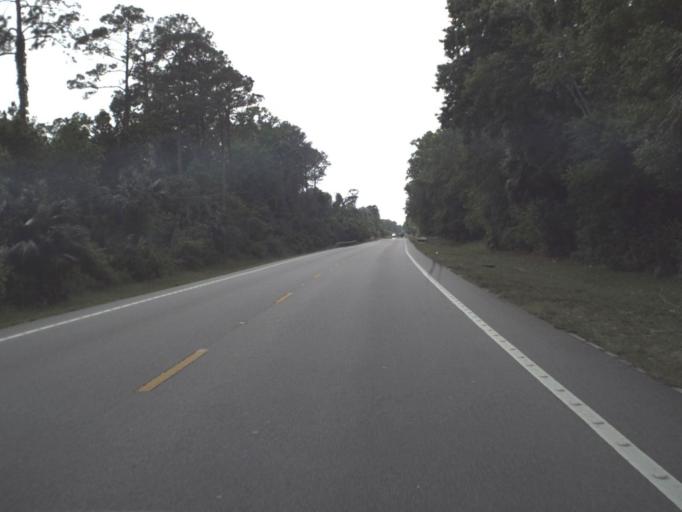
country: US
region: Florida
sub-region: Flagler County
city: Bunnell
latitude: 29.4669
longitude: -81.2899
